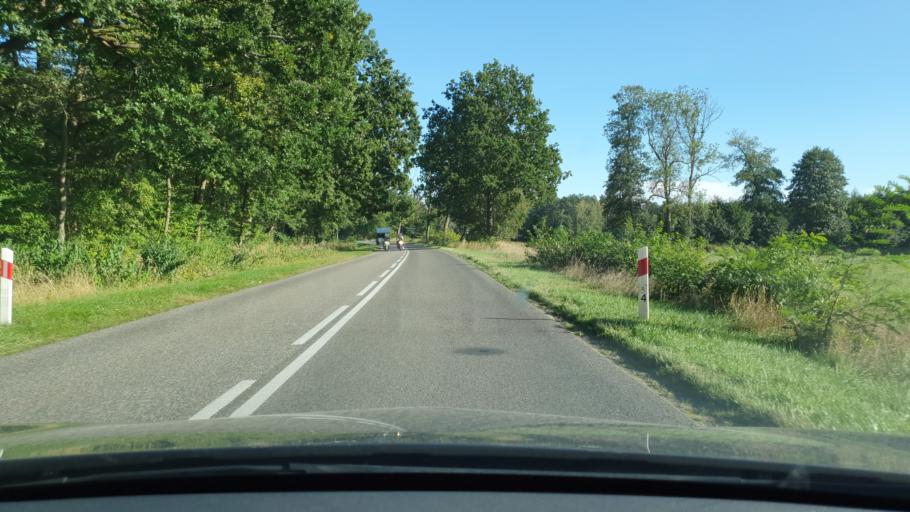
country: PL
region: West Pomeranian Voivodeship
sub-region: Powiat goleniowski
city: Przybiernow
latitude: 53.8288
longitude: 14.7785
